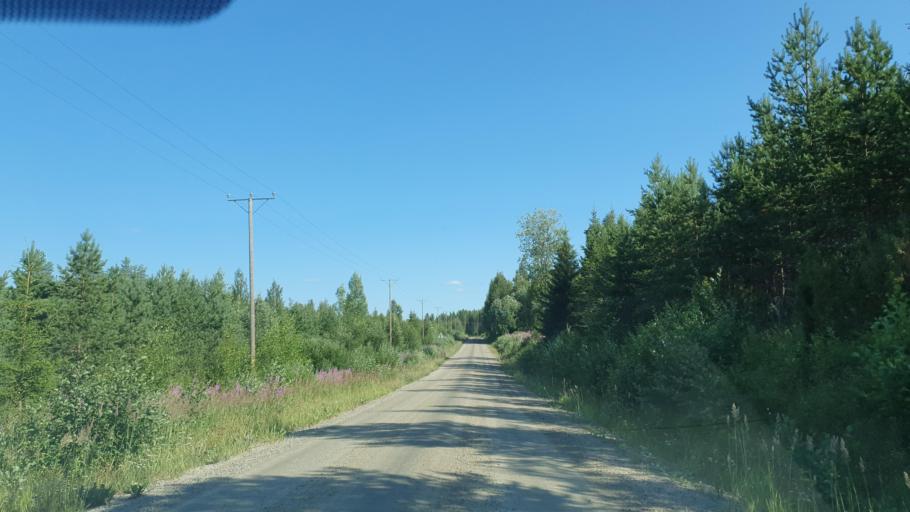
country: FI
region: Kainuu
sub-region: Kehys-Kainuu
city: Kuhmo
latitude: 64.0493
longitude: 29.6162
